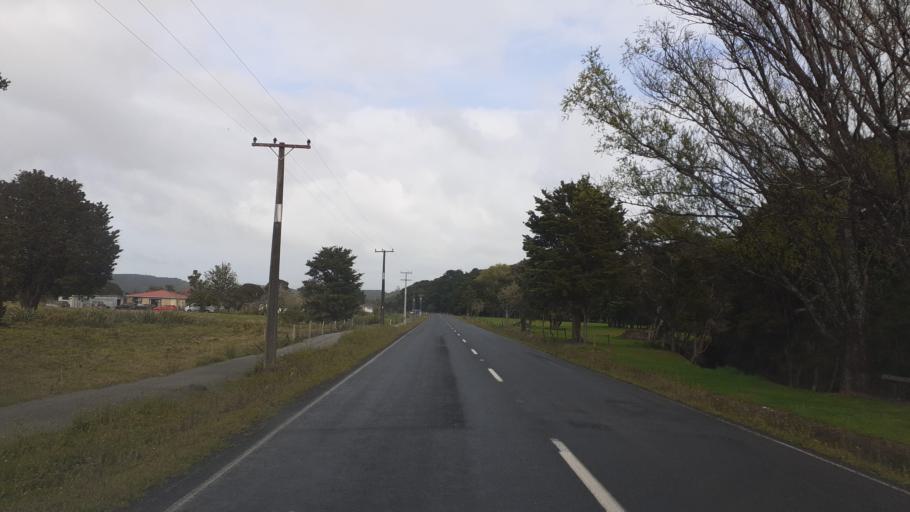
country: NZ
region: Northland
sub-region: Far North District
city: Moerewa
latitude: -35.3985
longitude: 173.9980
